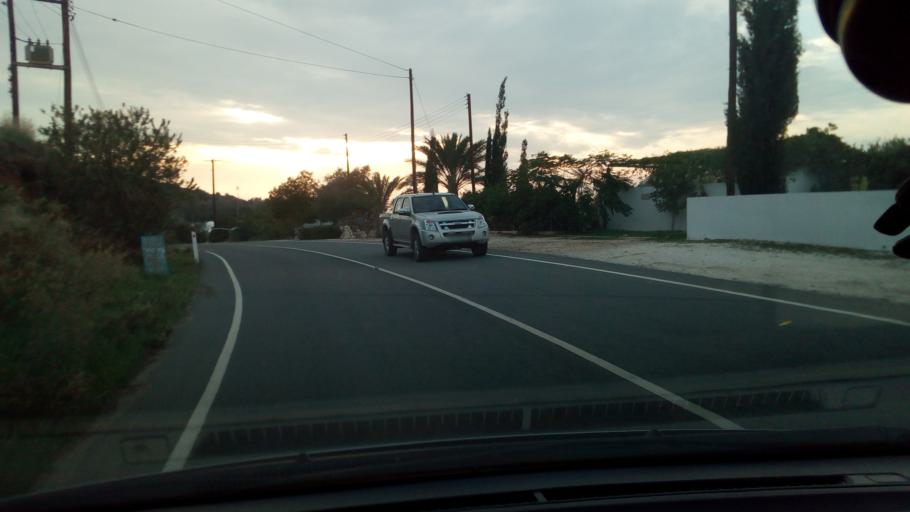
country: CY
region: Lefkosia
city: Kato Pyrgos
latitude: 35.1519
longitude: 32.5394
